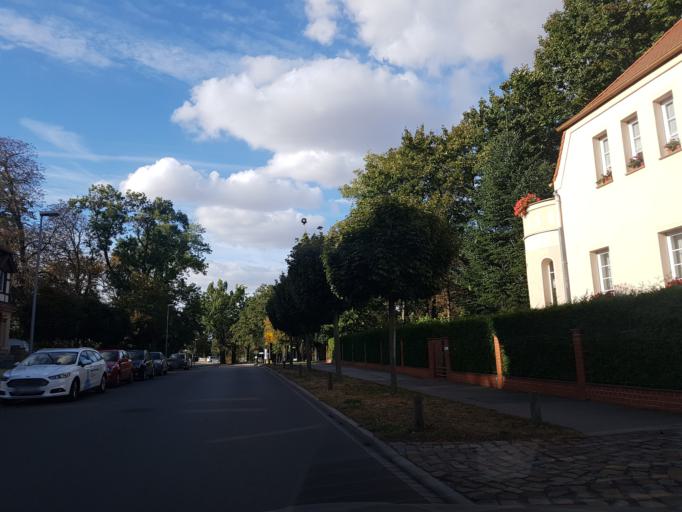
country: DE
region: Saxony
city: Torgau
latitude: 51.5635
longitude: 13.0001
